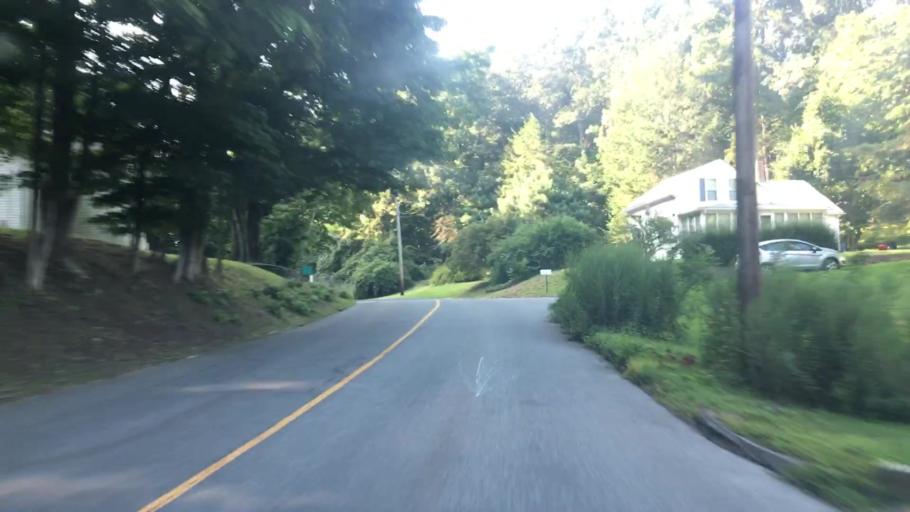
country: US
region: Connecticut
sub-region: Middlesex County
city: Deep River Center
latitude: 41.3909
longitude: -72.4466
